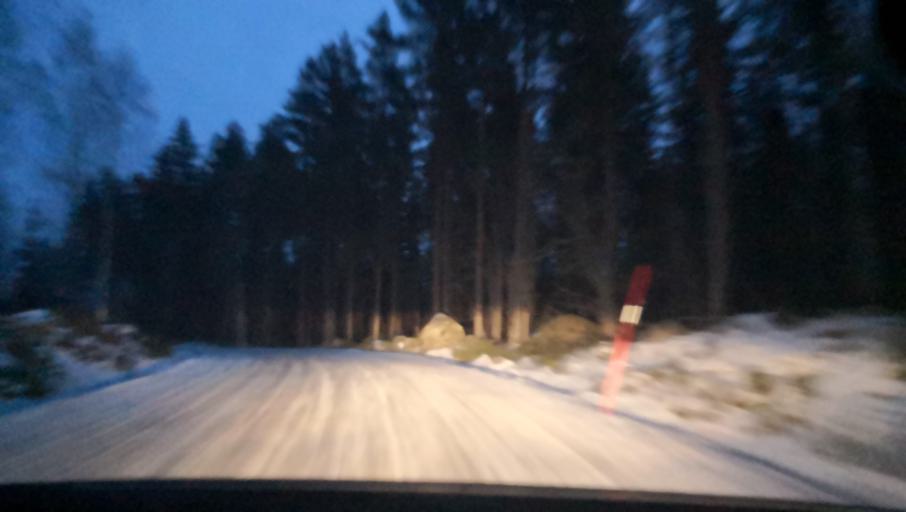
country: SE
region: Uppsala
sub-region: Heby Kommun
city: Tarnsjo
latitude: 60.2440
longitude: 16.7177
